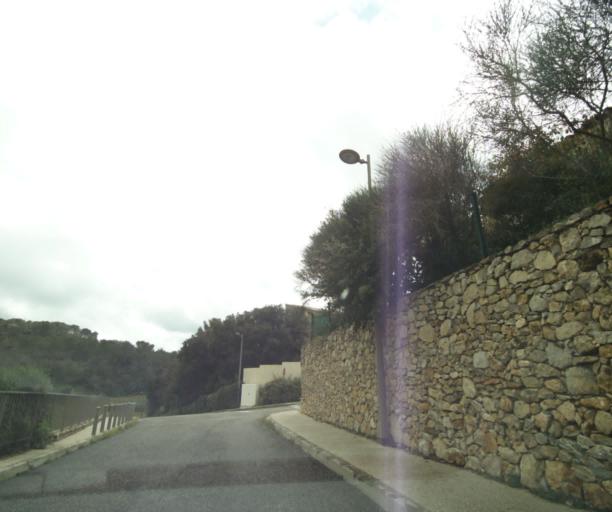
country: FR
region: Languedoc-Roussillon
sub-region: Departement de l'Herault
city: Murviel-les-Montpellier
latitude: 43.6016
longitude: 3.7353
